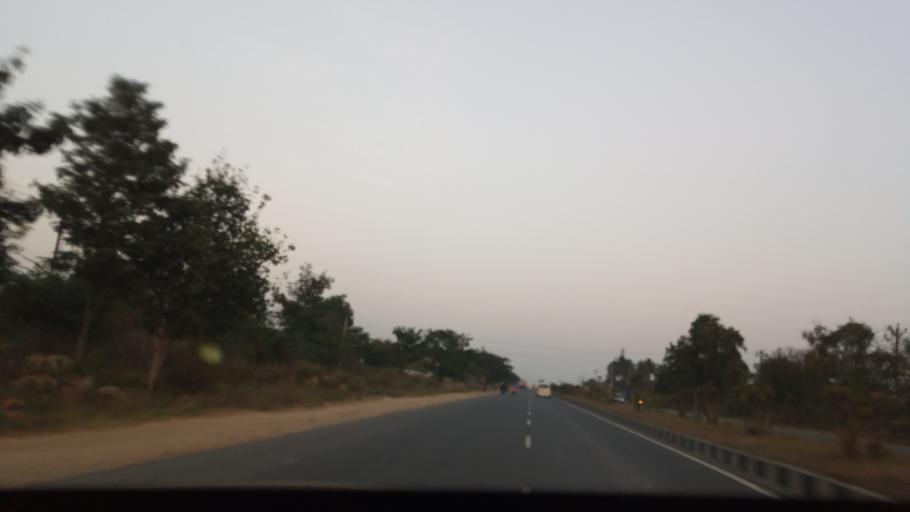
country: IN
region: Tamil Nadu
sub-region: Salem
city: Belur
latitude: 11.6648
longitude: 78.3006
